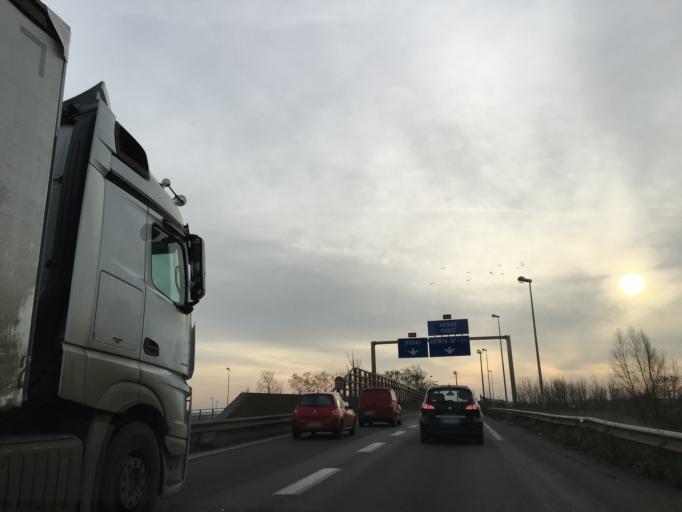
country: FR
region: Nord-Pas-de-Calais
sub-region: Departement du Pas-de-Calais
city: Dourges
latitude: 50.4268
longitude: 2.9802
